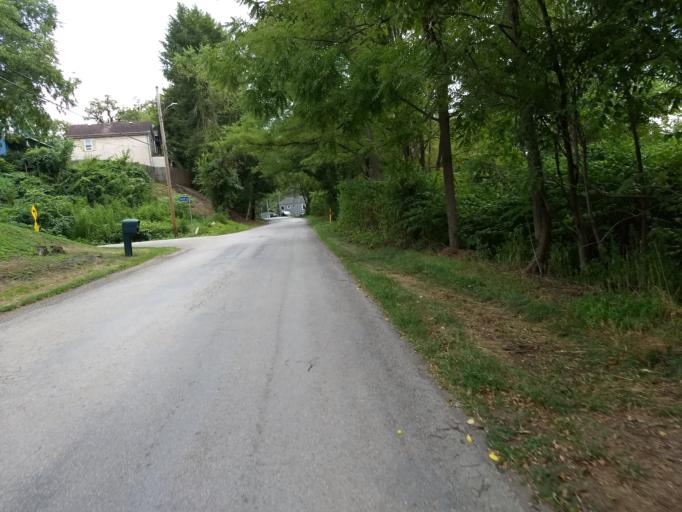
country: US
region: Pennsylvania
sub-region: Allegheny County
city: Brackenridge
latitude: 40.6136
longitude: -79.7113
